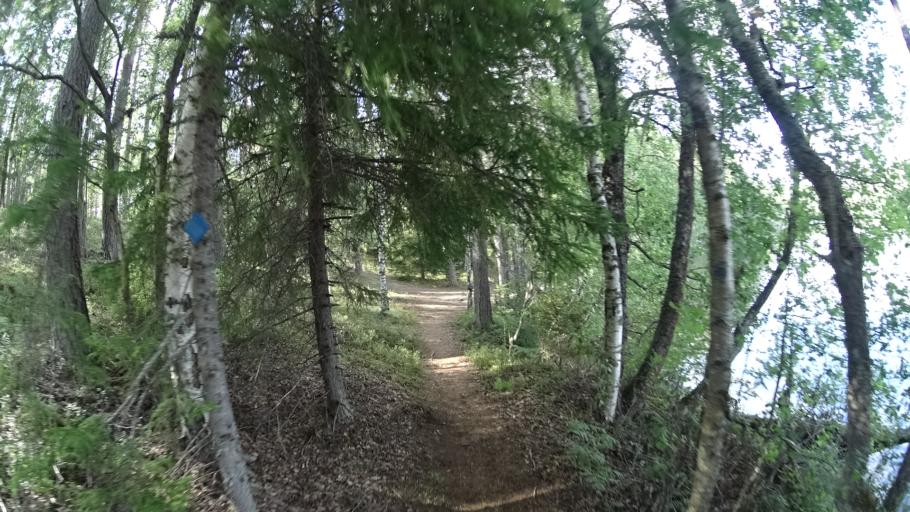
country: FI
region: Uusimaa
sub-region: Helsinki
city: Kaerkoelae
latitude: 60.7374
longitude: 24.0550
